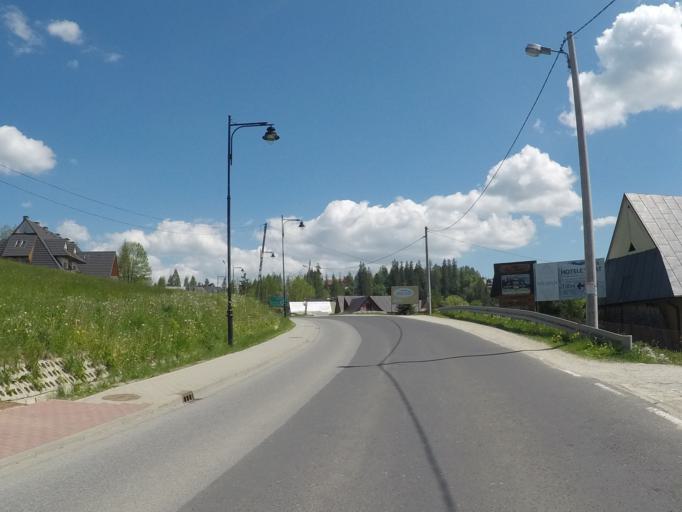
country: PL
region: Lesser Poland Voivodeship
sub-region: Powiat tatrzanski
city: Bukowina Tatrzanska
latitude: 49.3298
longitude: 20.0937
